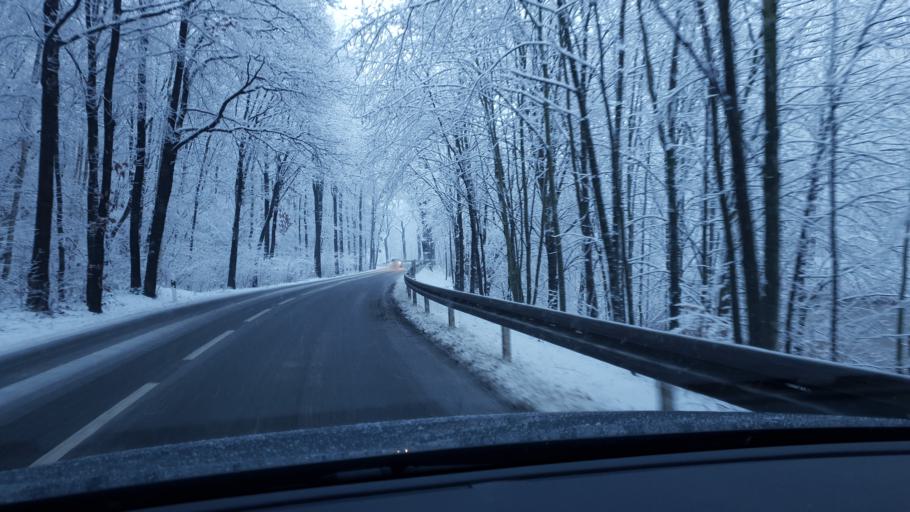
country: DE
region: Saxony
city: Taura
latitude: 50.9169
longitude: 12.8648
